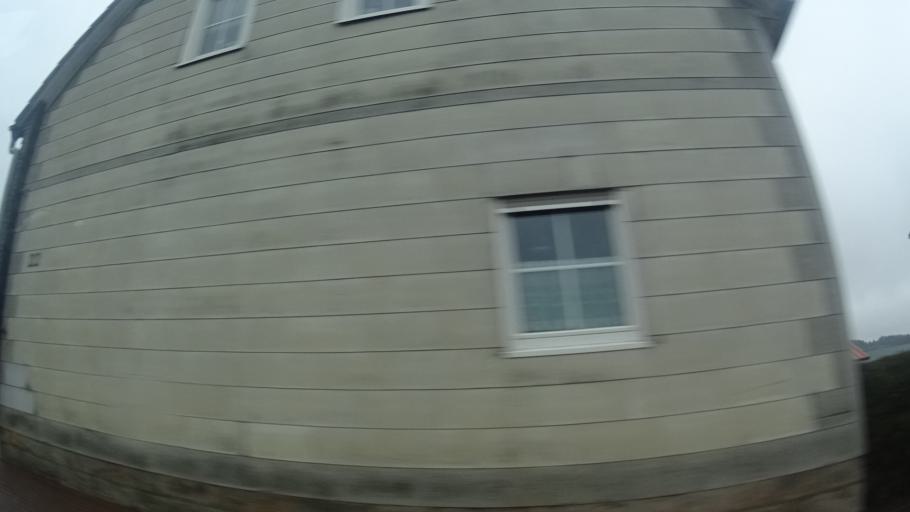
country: DE
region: Hesse
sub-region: Regierungsbezirk Kassel
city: Eichenzell
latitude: 50.4778
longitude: 9.7415
